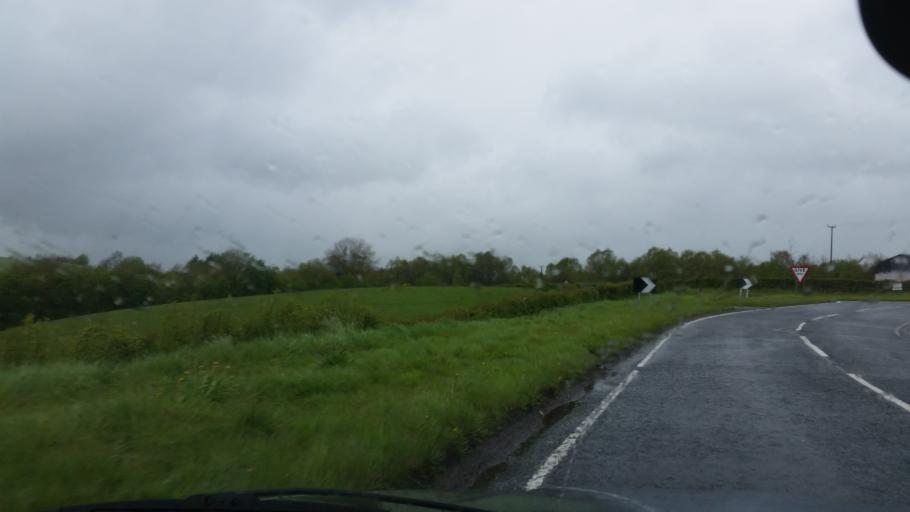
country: GB
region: Northern Ireland
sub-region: Omagh District
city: Omagh
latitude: 54.5619
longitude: -7.2759
